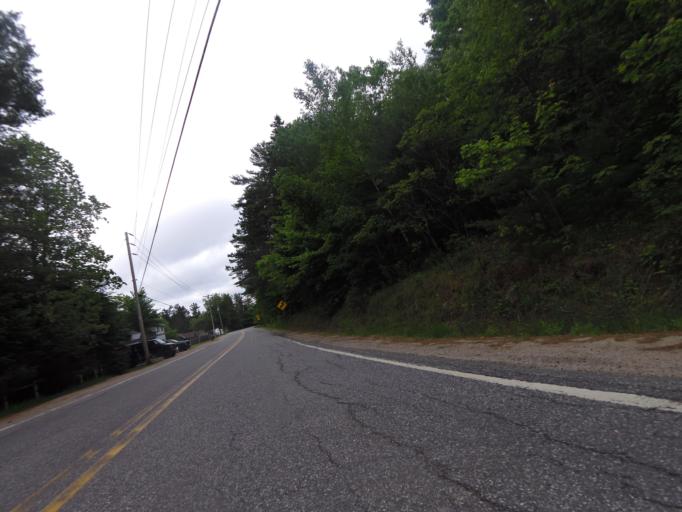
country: CA
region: Quebec
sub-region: Outaouais
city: Shawville
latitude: 45.8563
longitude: -76.4266
